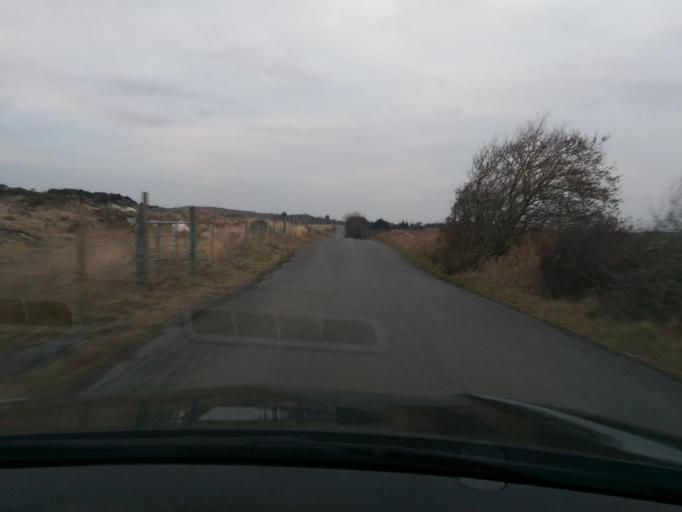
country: IE
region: Connaught
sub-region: County Galway
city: Bearna
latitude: 53.2841
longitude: -9.1635
